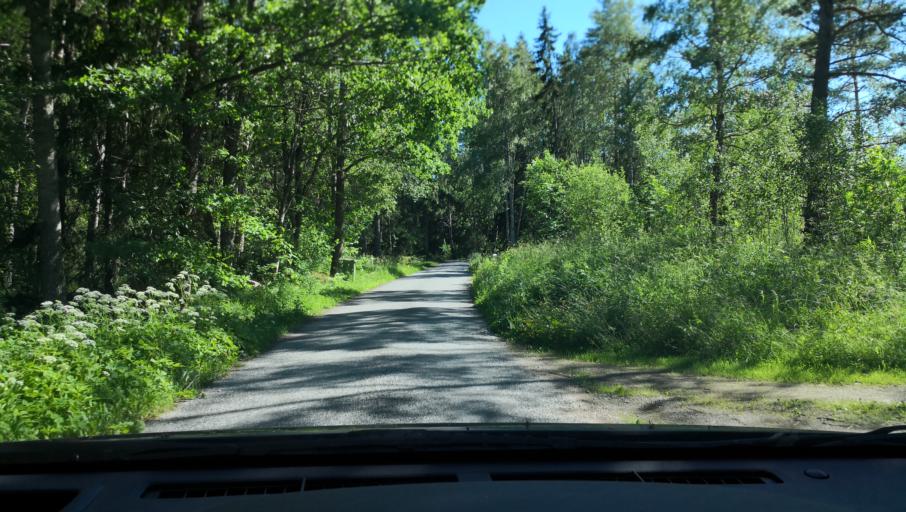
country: SE
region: Soedermanland
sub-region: Eskilstuna Kommun
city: Arla
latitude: 59.3269
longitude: 16.5965
